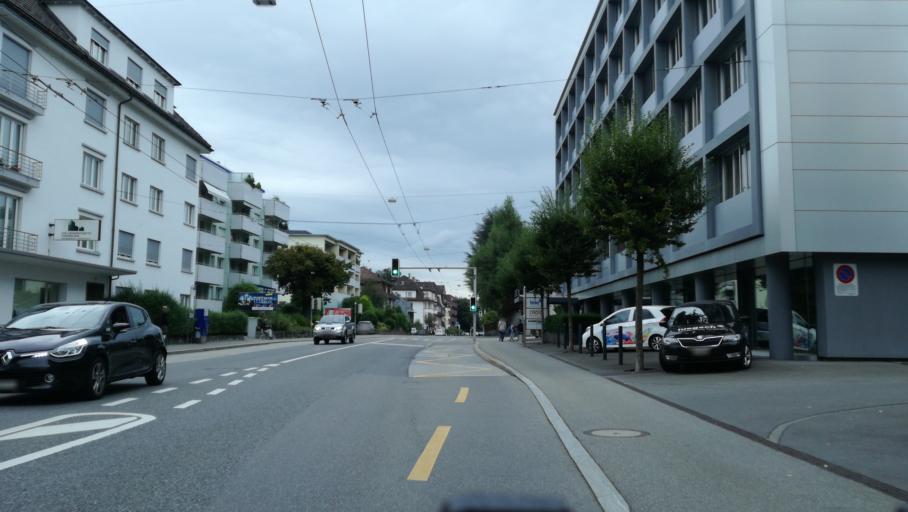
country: CH
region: Lucerne
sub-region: Lucerne-Stadt District
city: Luzern
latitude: 47.0653
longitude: 8.3117
